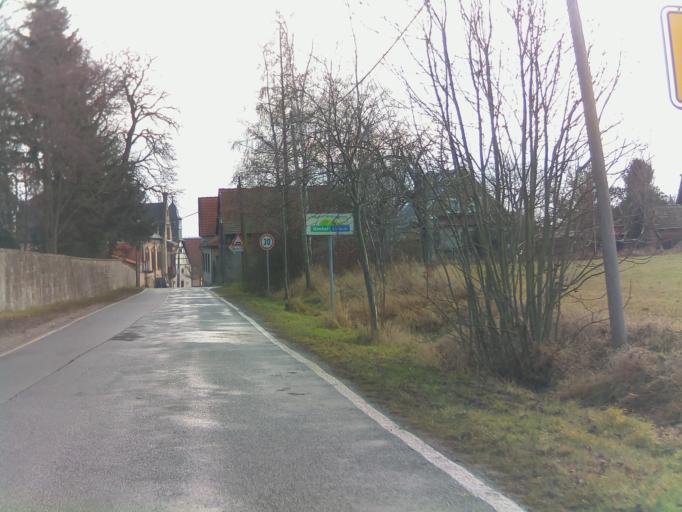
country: DE
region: Thuringia
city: Bad Berka
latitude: 50.9199
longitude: 11.2800
